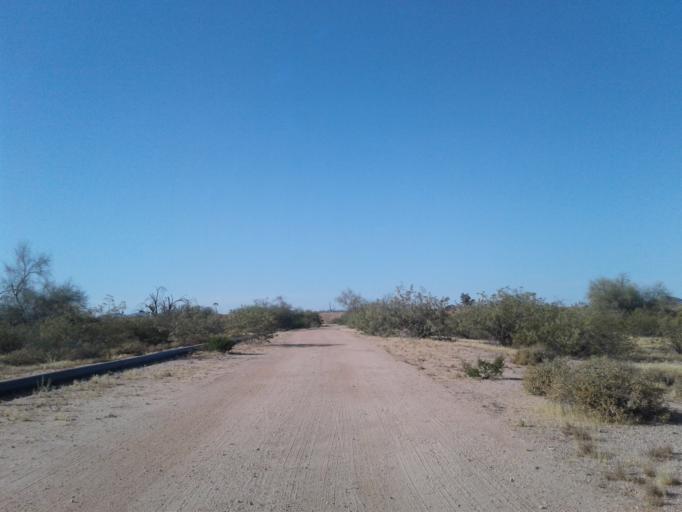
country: US
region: Arizona
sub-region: Maricopa County
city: Paradise Valley
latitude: 33.6796
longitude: -112.0138
